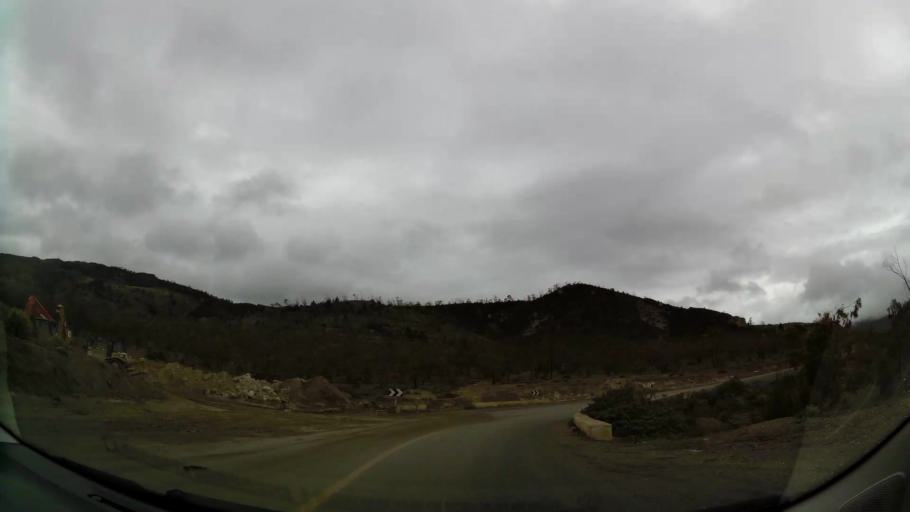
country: MA
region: Taza-Al Hoceima-Taounate
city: Imzourene
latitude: 34.9374
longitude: -3.8100
